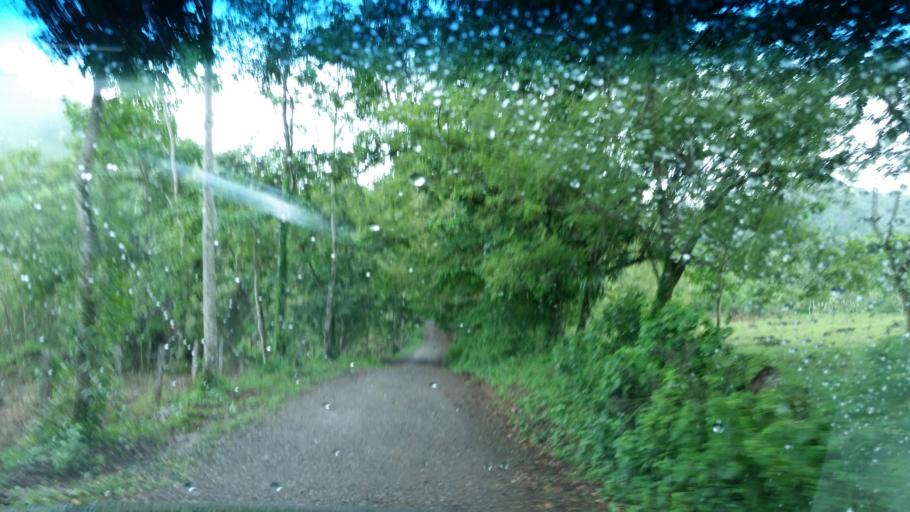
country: NI
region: Atlantico Norte (RAAN)
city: Waslala
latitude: 13.1650
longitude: -85.4175
